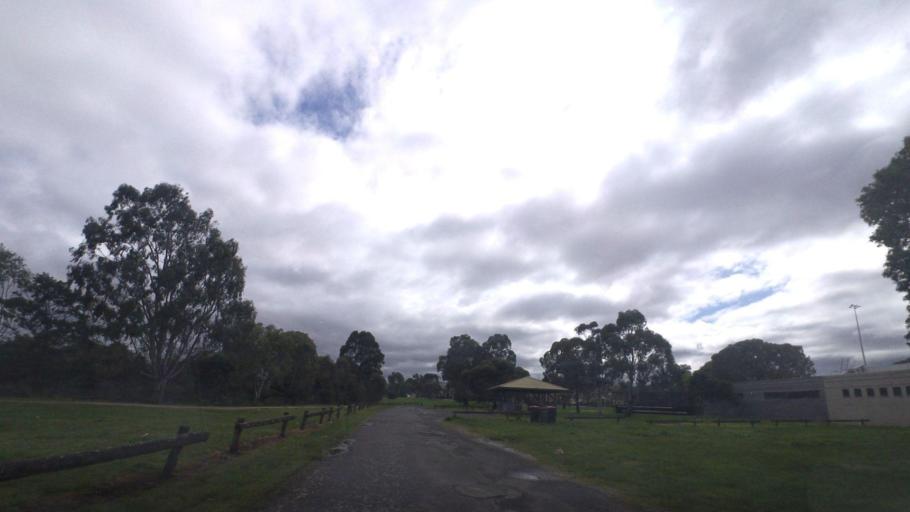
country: AU
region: Victoria
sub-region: Banyule
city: Bundoora
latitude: -37.7073
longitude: 145.0487
